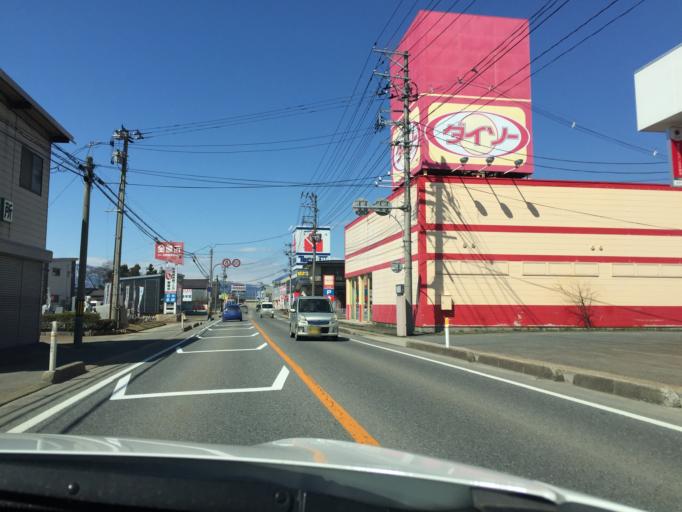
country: JP
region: Yamagata
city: Nagai
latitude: 38.0882
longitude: 140.0427
